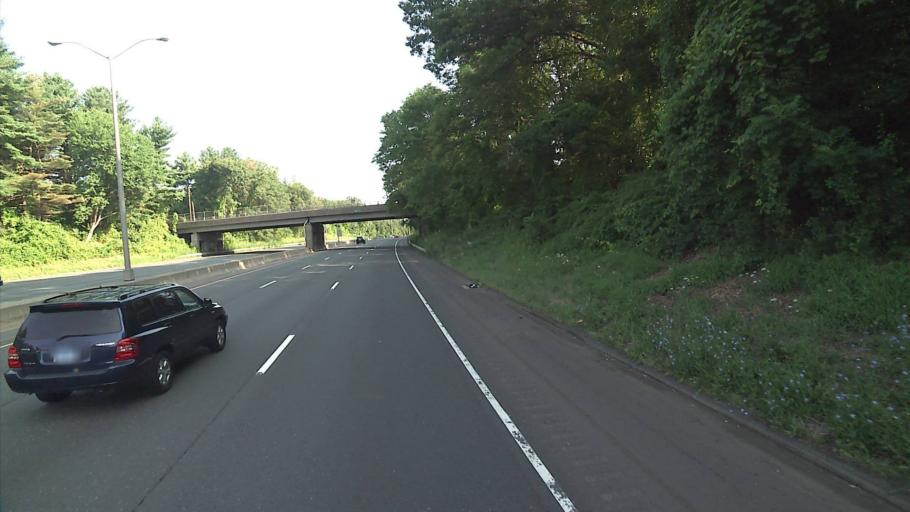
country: US
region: Connecticut
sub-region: Hartford County
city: Sherwood Manor
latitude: 42.0231
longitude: -72.5890
